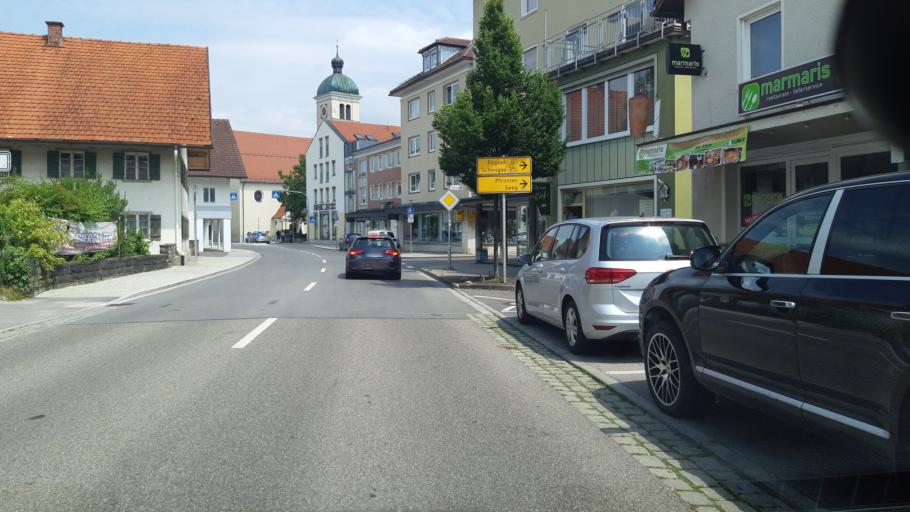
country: DE
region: Bavaria
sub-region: Swabia
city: Marktoberdorf
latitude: 47.7771
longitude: 10.6179
